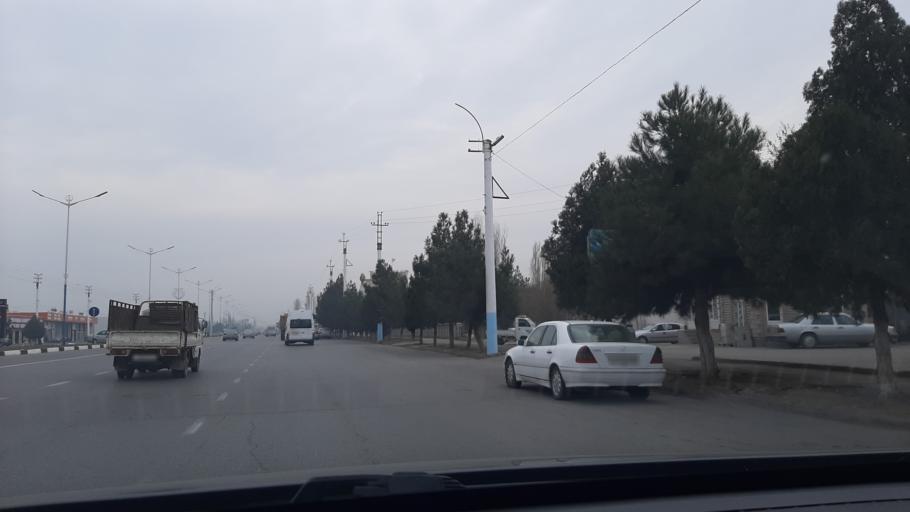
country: TJ
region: Viloyati Sughd
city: Chkalov
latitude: 40.2418
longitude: 69.7058
